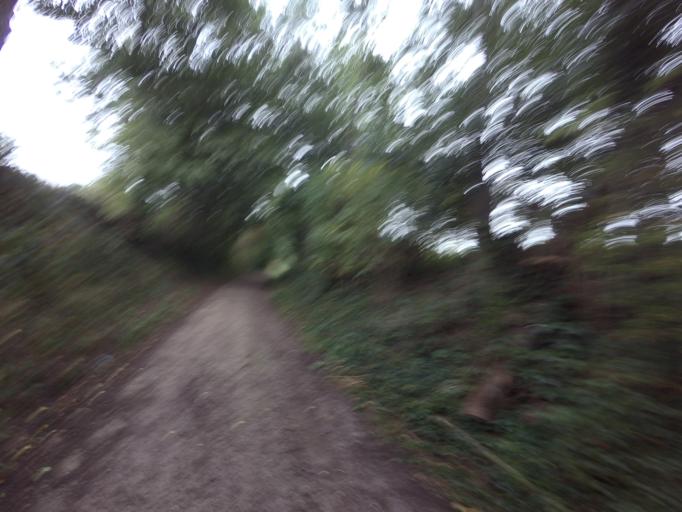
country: NL
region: Limburg
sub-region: Eijsden-Margraten
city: Margraten
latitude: 50.8233
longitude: 5.7955
